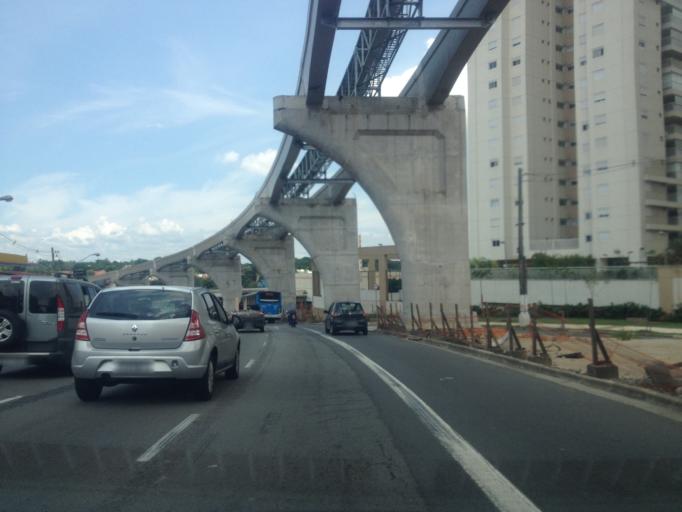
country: BR
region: Sao Paulo
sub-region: Diadema
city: Diadema
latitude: -23.6294
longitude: -46.6675
